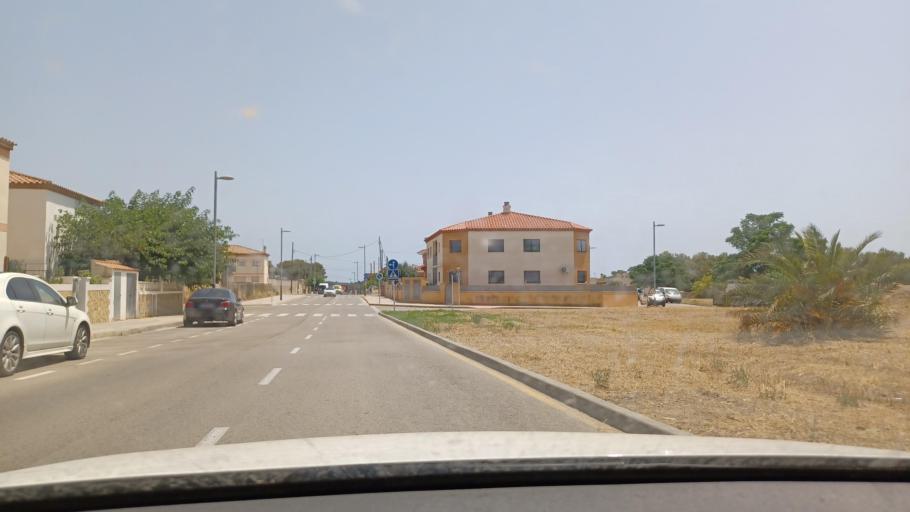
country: ES
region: Catalonia
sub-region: Provincia de Tarragona
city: Colldejou
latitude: 41.0024
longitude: 0.9271
